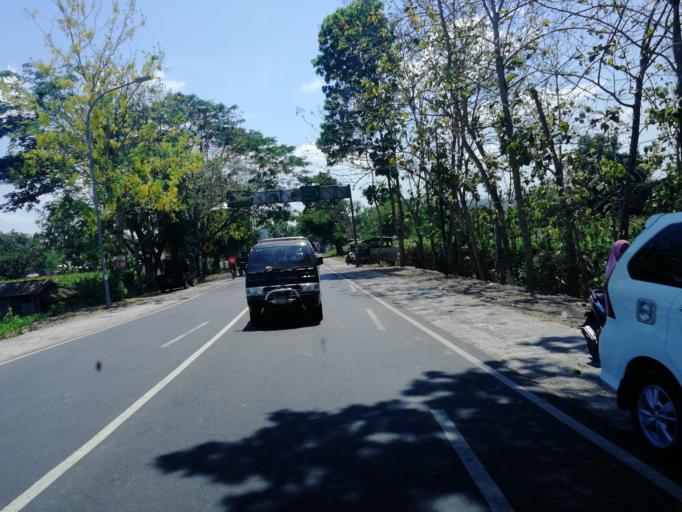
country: ID
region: West Nusa Tenggara
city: Kediri
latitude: -8.6894
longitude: 116.1147
